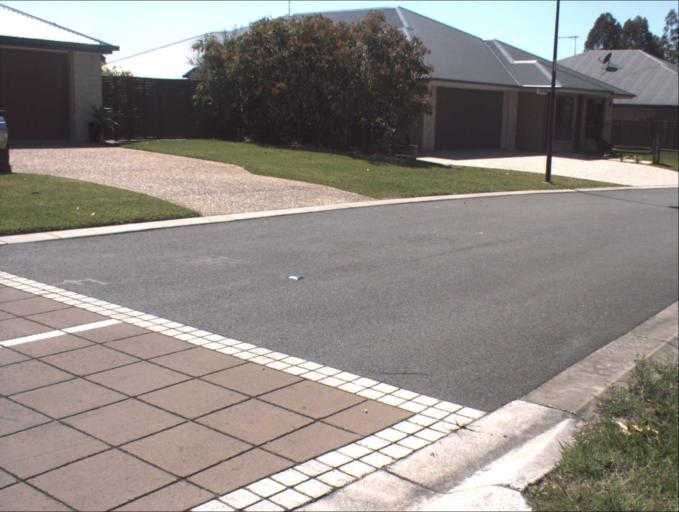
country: AU
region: Queensland
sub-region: Logan
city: Waterford West
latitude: -27.7139
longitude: 153.1445
